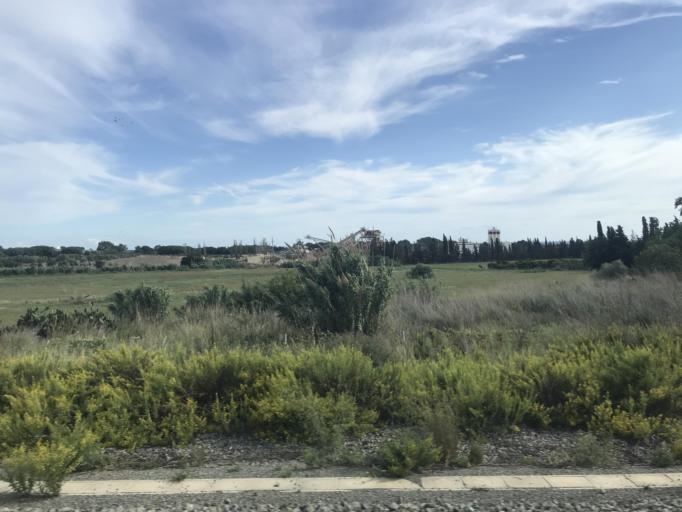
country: ES
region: Catalonia
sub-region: Provincia de Tarragona
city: Cambrils
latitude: 41.0908
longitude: 1.0750
